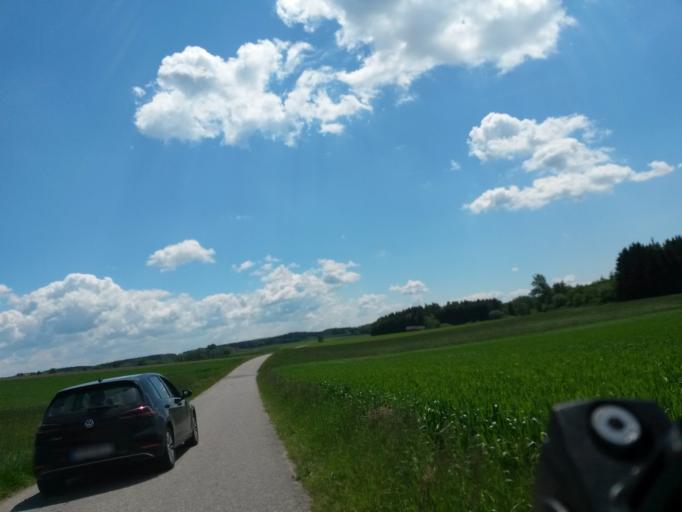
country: DE
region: Baden-Wuerttemberg
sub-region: Tuebingen Region
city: Ingoldingen
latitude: 47.9783
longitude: 9.7136
